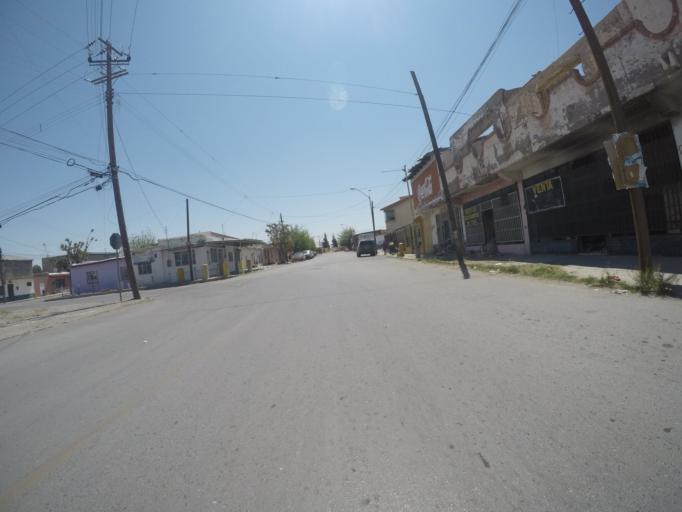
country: MX
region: Chihuahua
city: Ciudad Juarez
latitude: 31.7238
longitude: -106.4824
